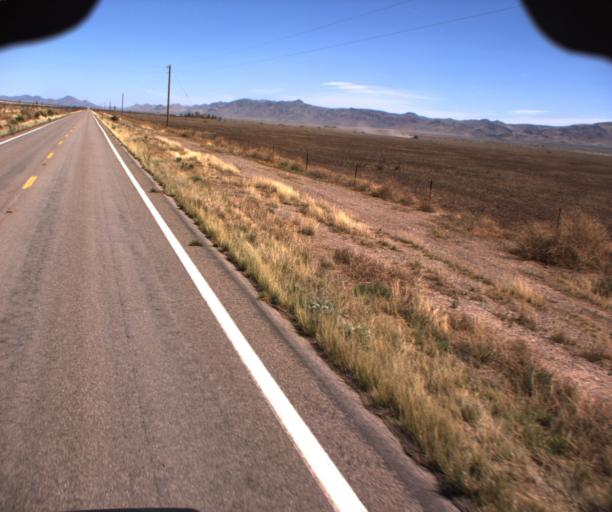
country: US
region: Arizona
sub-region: Cochise County
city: Douglas
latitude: 31.7208
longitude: -109.1118
